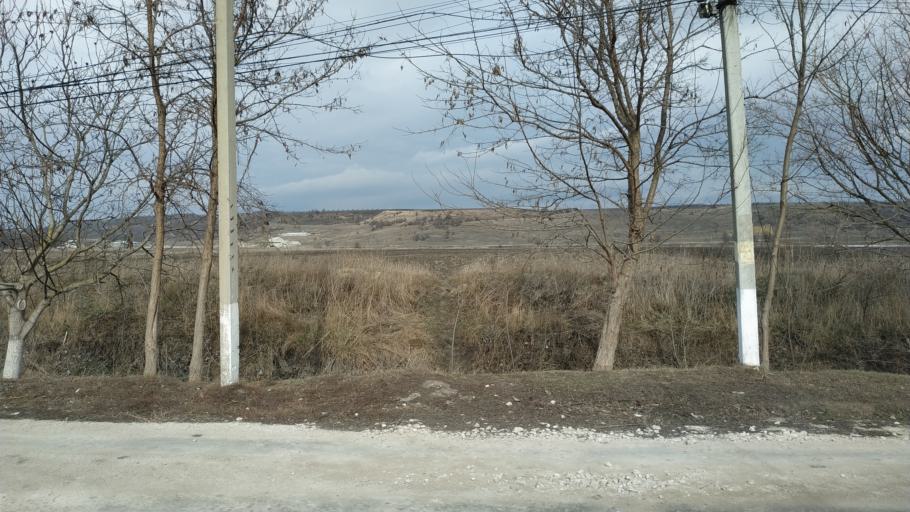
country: MD
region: Laloveni
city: Ialoveni
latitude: 46.8579
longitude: 28.7896
